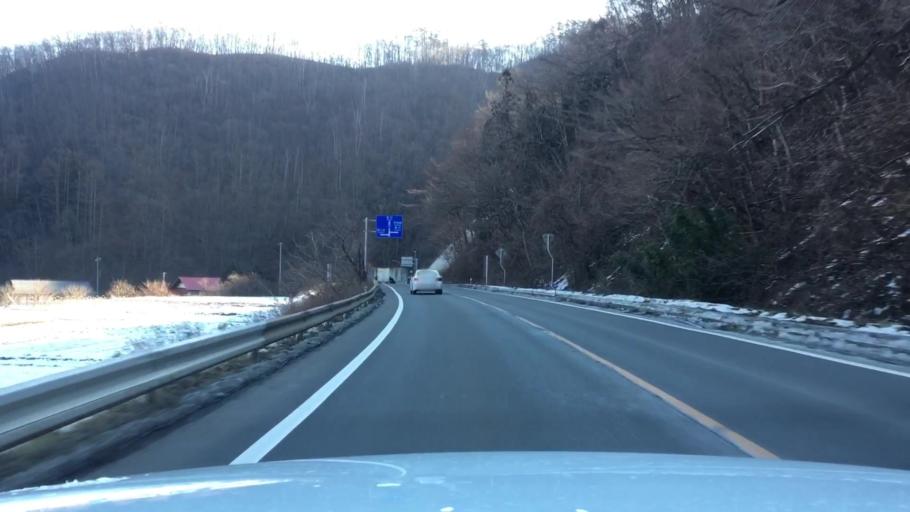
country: JP
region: Iwate
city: Tono
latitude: 39.6230
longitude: 141.6126
